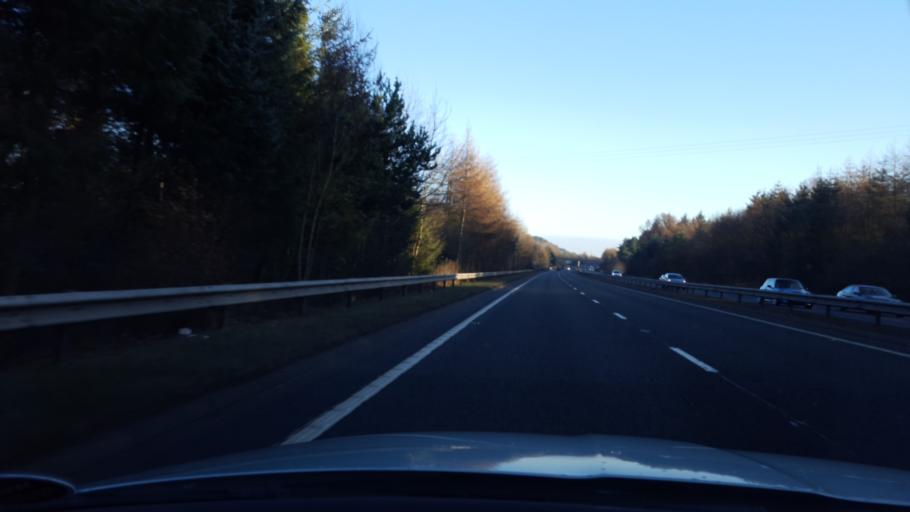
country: GB
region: Scotland
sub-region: Fife
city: Cardenden
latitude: 56.1303
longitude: -3.2514
